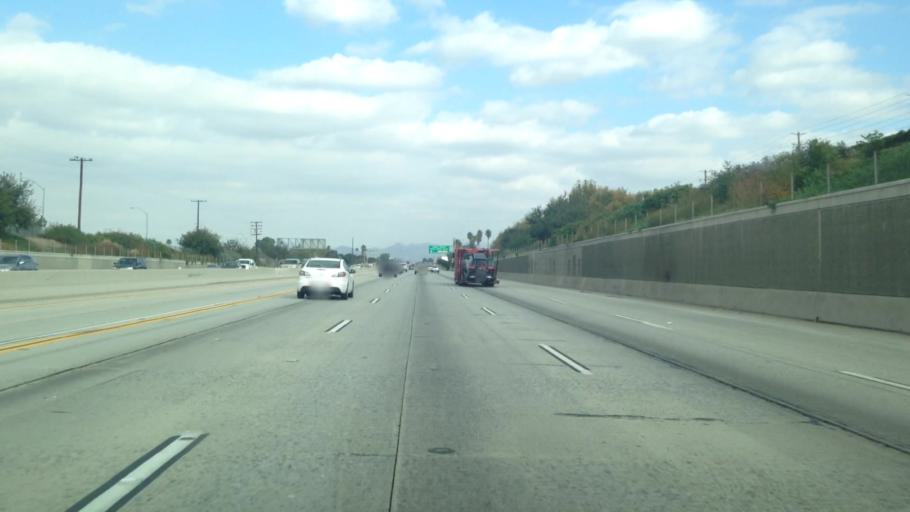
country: US
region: California
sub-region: Riverside County
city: Riverside
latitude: 33.9196
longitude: -117.4332
